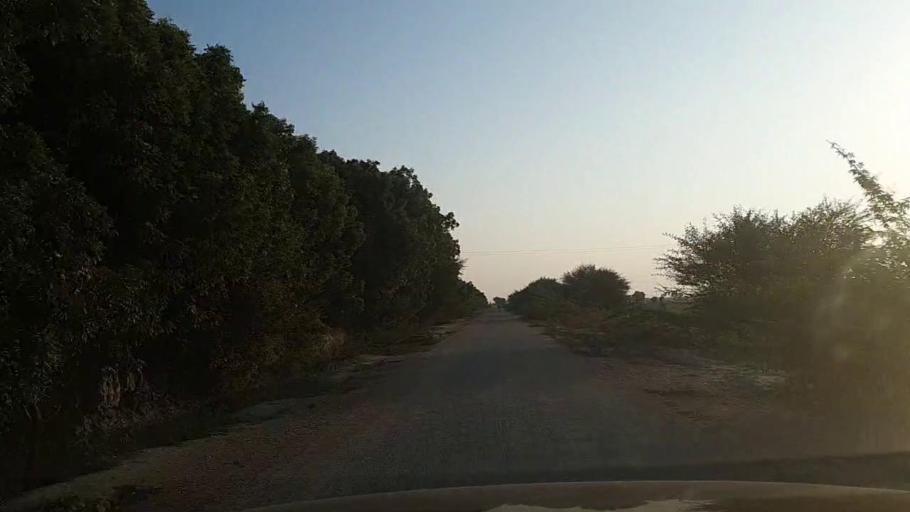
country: PK
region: Sindh
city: Naukot
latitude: 24.8417
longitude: 69.3122
